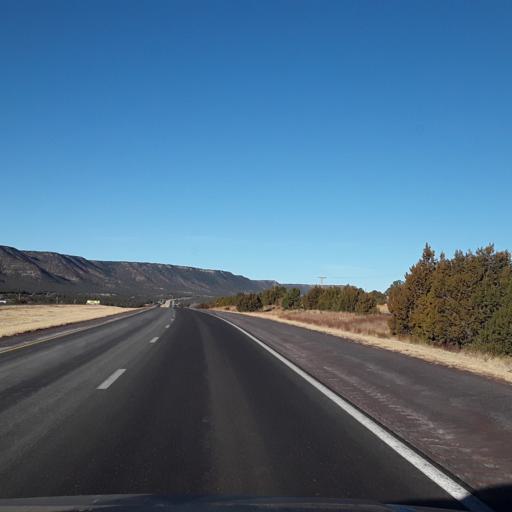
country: US
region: New Mexico
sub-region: San Miguel County
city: Pecos
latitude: 35.4214
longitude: -105.5527
